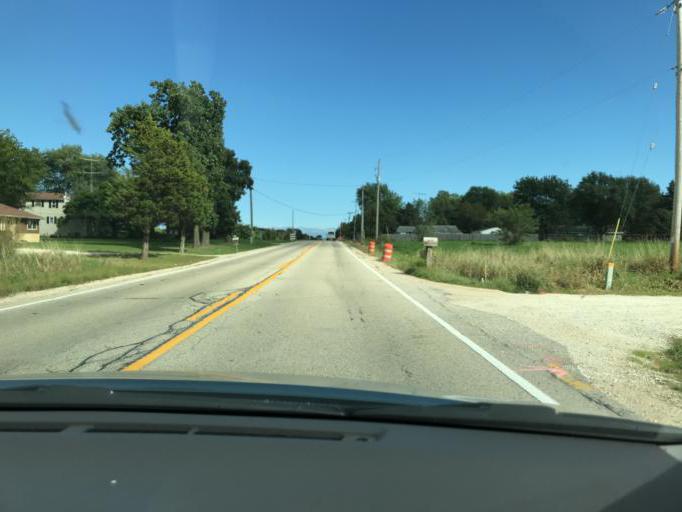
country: US
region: Wisconsin
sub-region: Kenosha County
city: Pleasant Prairie
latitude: 42.5227
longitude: -87.8753
